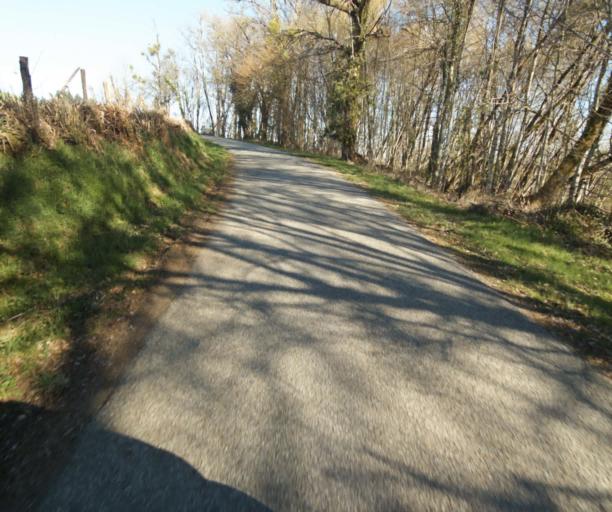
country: FR
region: Limousin
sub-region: Departement de la Correze
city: Chamboulive
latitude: 45.4038
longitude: 1.7207
